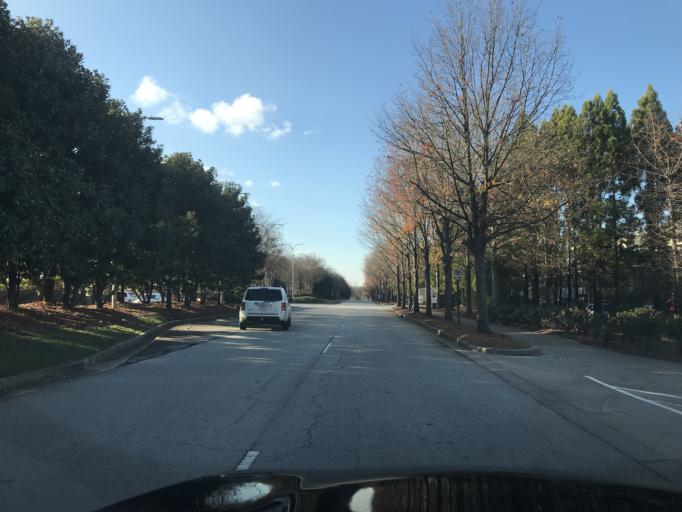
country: US
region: Georgia
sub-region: Fulton County
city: College Park
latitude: 33.6443
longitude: -84.4573
